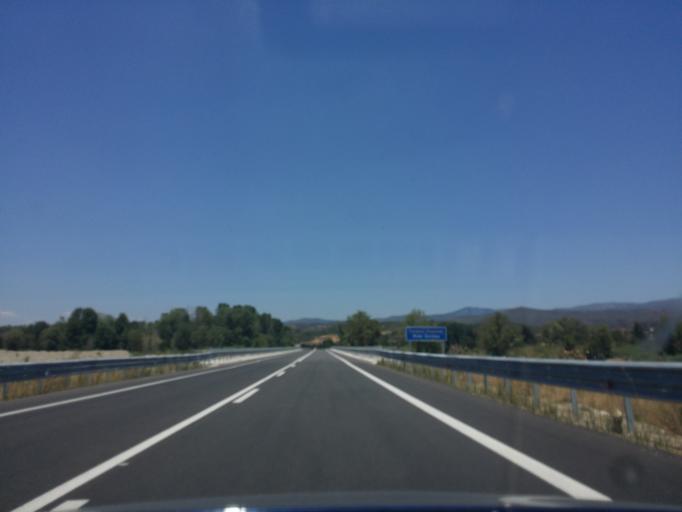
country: GR
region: Peloponnese
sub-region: Nomos Lakonias
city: Sparti
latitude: 37.0104
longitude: 22.4845
